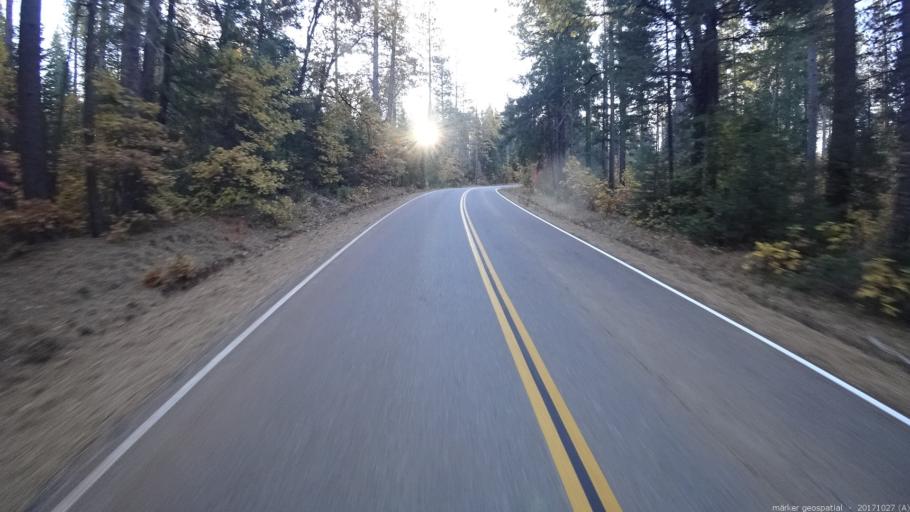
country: US
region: California
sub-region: Shasta County
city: Burney
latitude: 40.9308
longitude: -121.9425
